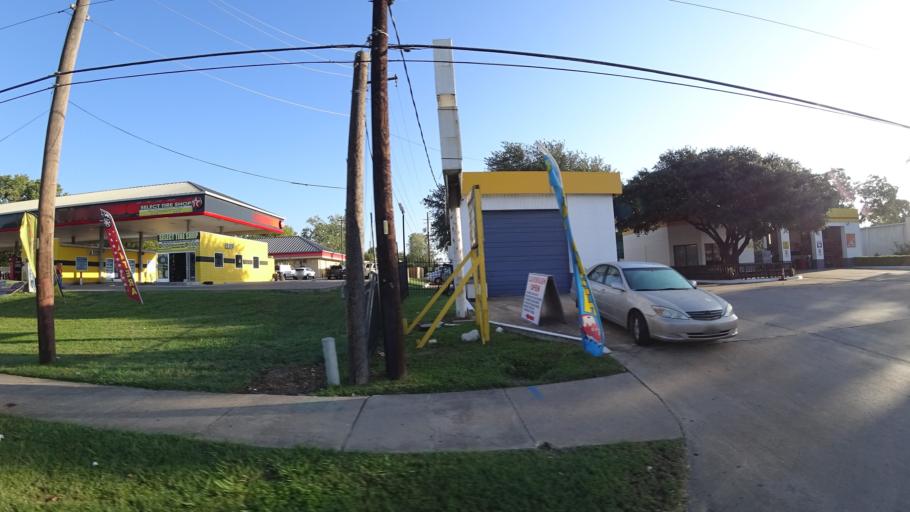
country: US
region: Texas
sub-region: Travis County
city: Wells Branch
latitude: 30.3593
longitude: -97.6902
